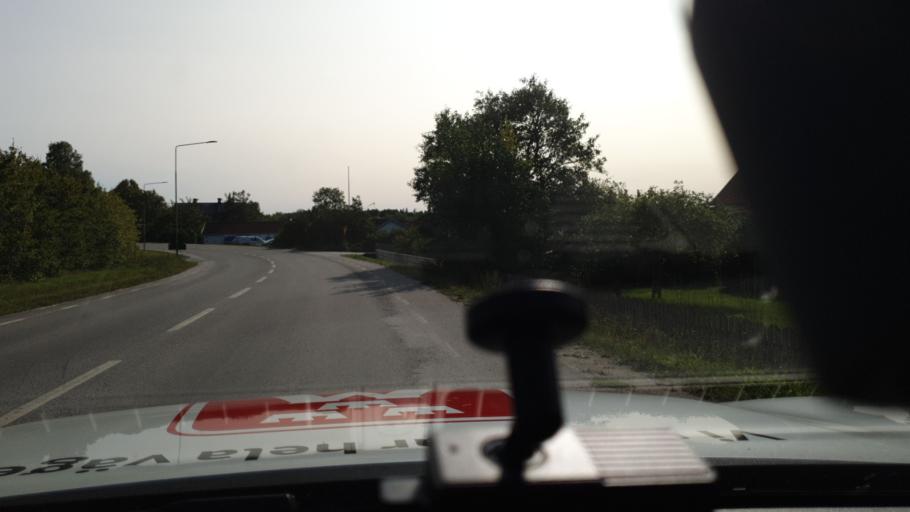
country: SE
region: Gotland
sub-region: Gotland
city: Slite
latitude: 57.7239
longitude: 18.7884
